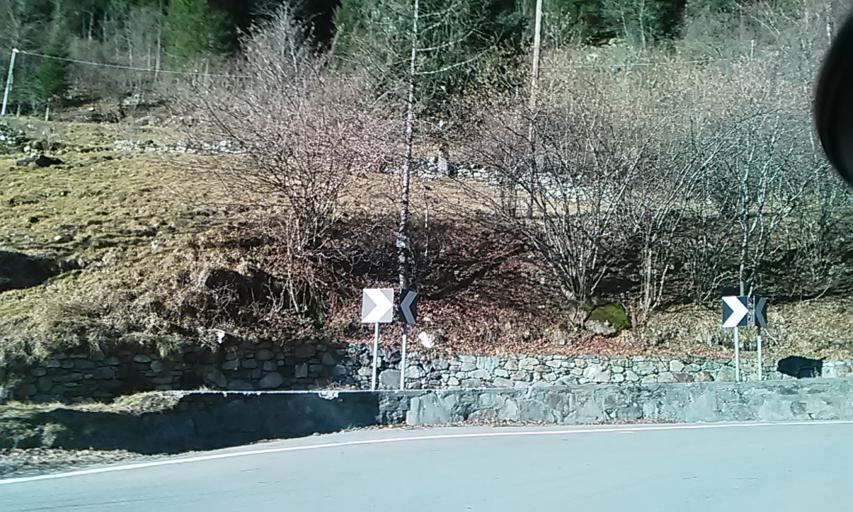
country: IT
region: Piedmont
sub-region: Provincia di Vercelli
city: Rimasco
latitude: 45.8701
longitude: 8.0677
